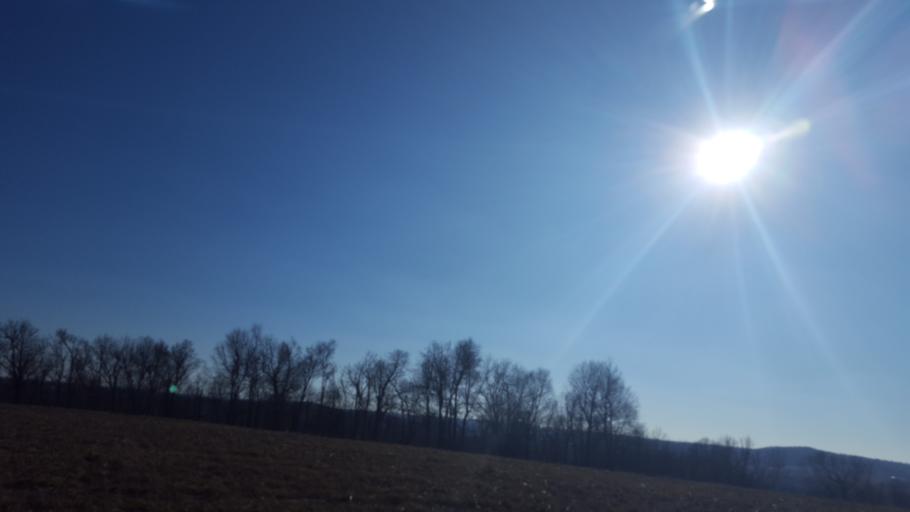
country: US
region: Kentucky
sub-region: Crittenden County
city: Marion
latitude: 37.4475
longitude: -88.0838
